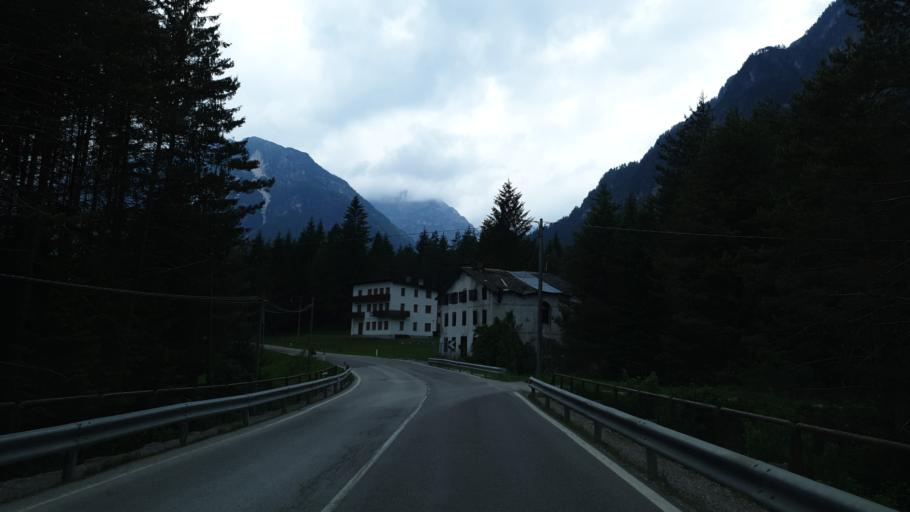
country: IT
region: Veneto
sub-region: Provincia di Belluno
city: Auronzo
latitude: 46.5777
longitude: 12.3845
